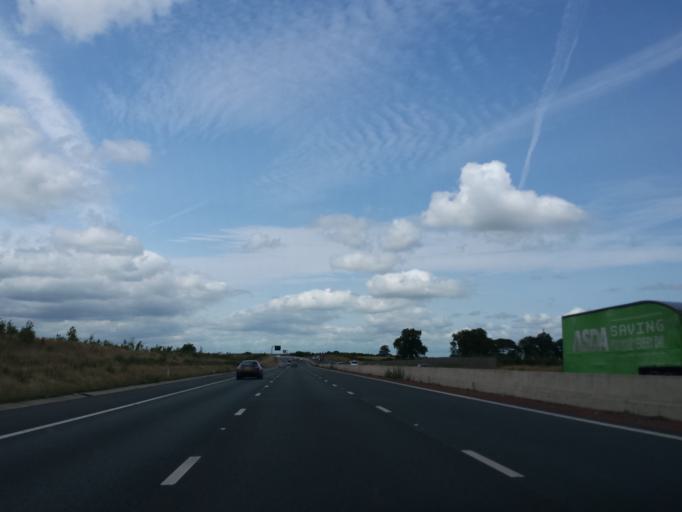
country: GB
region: England
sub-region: North Yorkshire
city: Bedale
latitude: 54.2637
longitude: -1.5187
